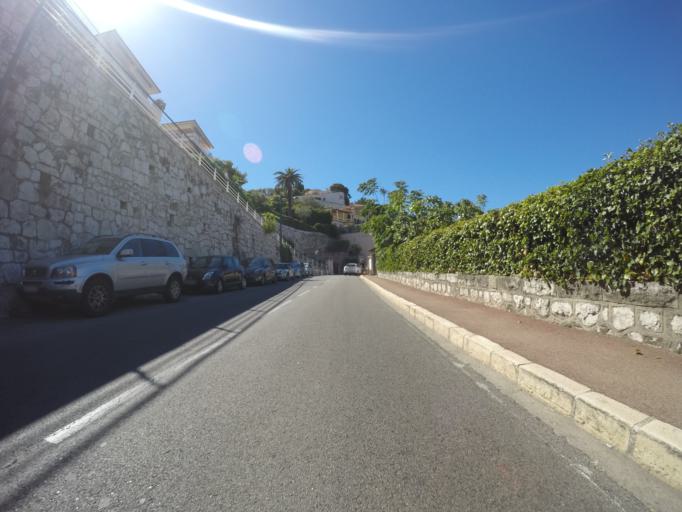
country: FR
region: Provence-Alpes-Cote d'Azur
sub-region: Departement des Alpes-Maritimes
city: Beaulieu-sur-Mer
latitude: 43.7002
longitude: 7.3266
